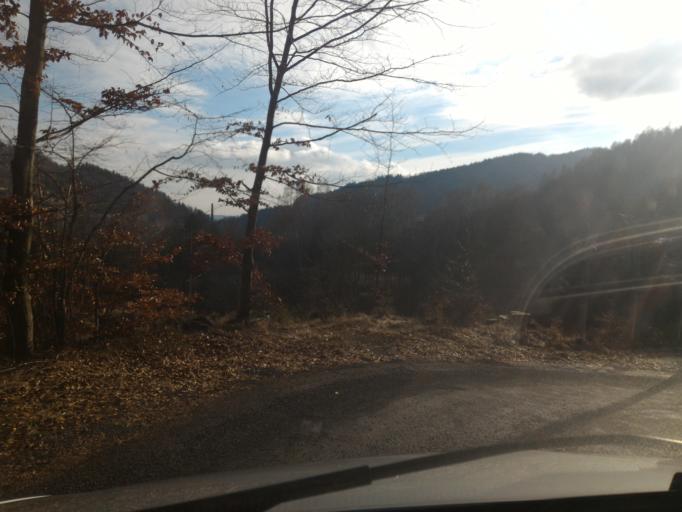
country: CZ
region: Liberecky
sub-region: Okres Jablonec nad Nisou
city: Tanvald
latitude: 50.7447
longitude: 15.3081
